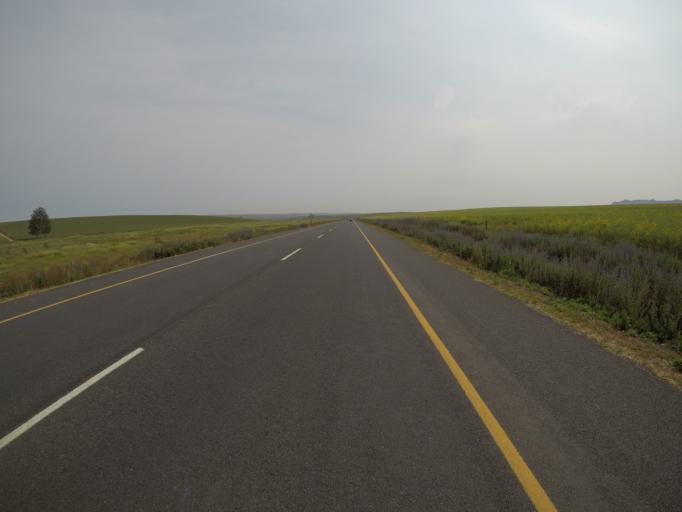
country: ZA
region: Western Cape
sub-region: West Coast District Municipality
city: Malmesbury
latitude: -33.4664
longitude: 18.7903
